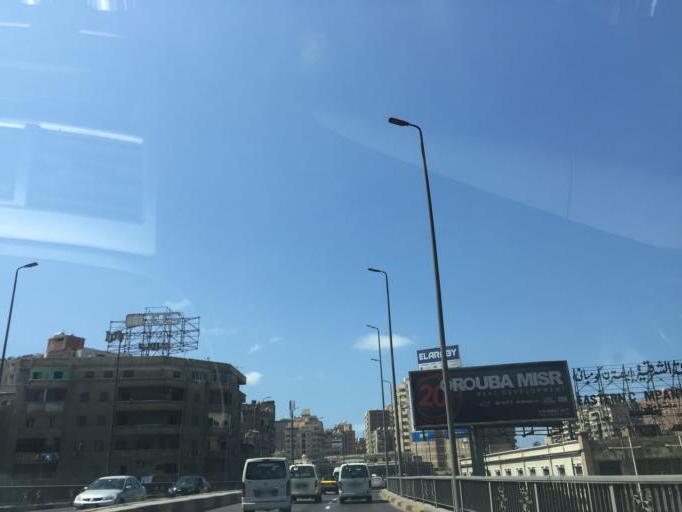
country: EG
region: Alexandria
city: Alexandria
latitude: 31.1886
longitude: 29.9240
